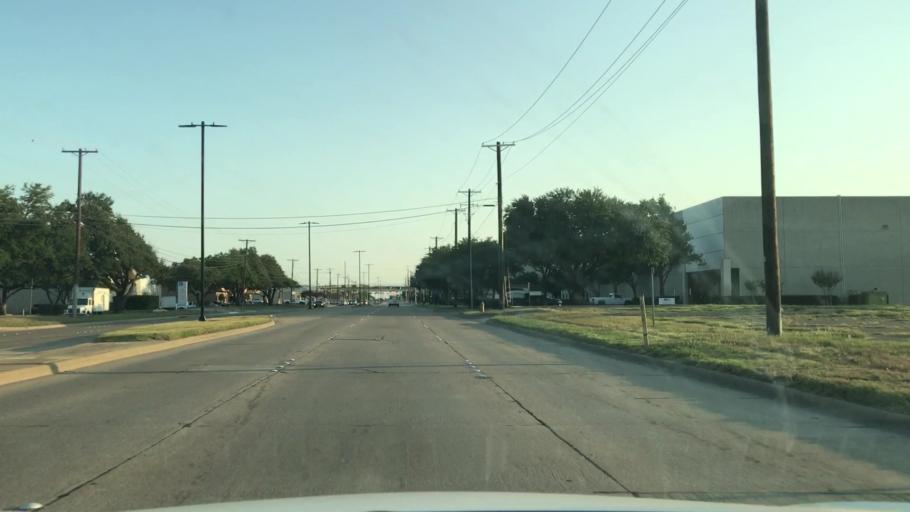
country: US
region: Texas
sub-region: Dallas County
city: Garland
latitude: 32.9023
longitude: -96.6829
